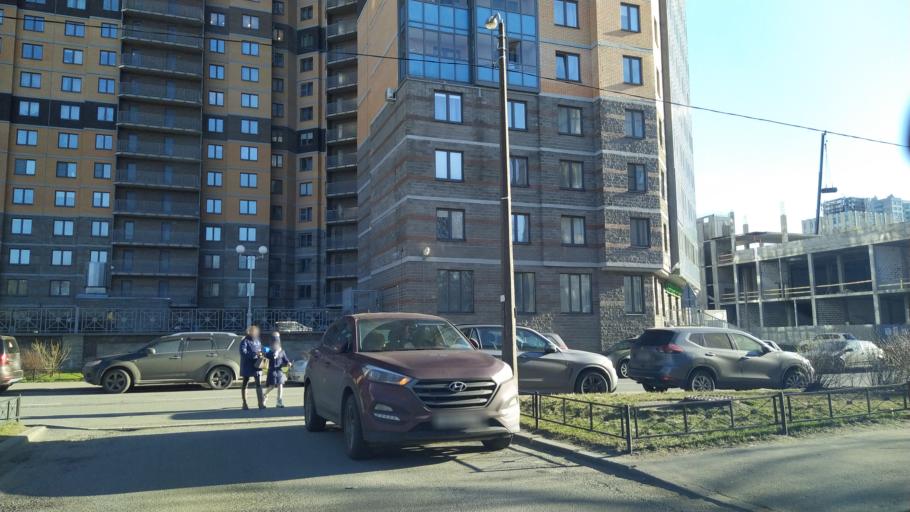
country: RU
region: St.-Petersburg
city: Grazhdanka
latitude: 60.0402
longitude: 30.4067
